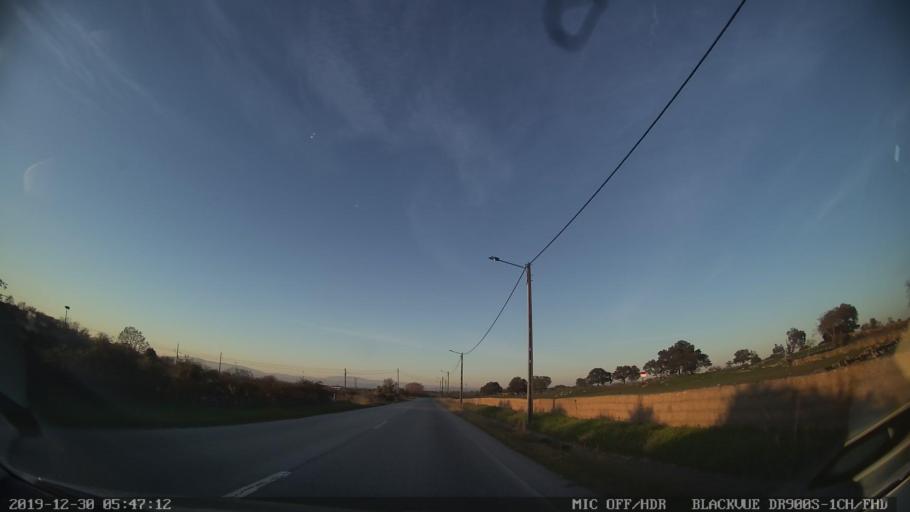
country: PT
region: Castelo Branco
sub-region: Idanha-A-Nova
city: Idanha-a-Nova
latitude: 39.9484
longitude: -7.2384
